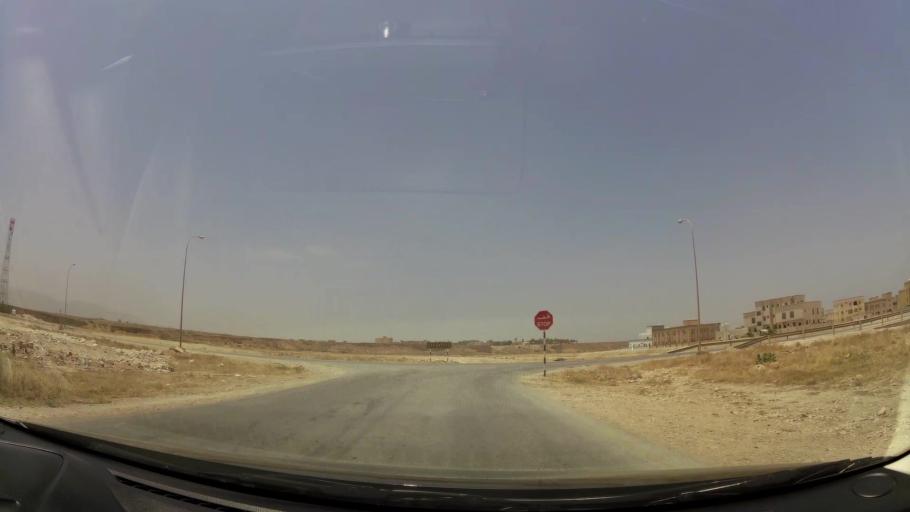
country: OM
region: Zufar
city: Salalah
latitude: 17.0844
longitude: 54.1607
